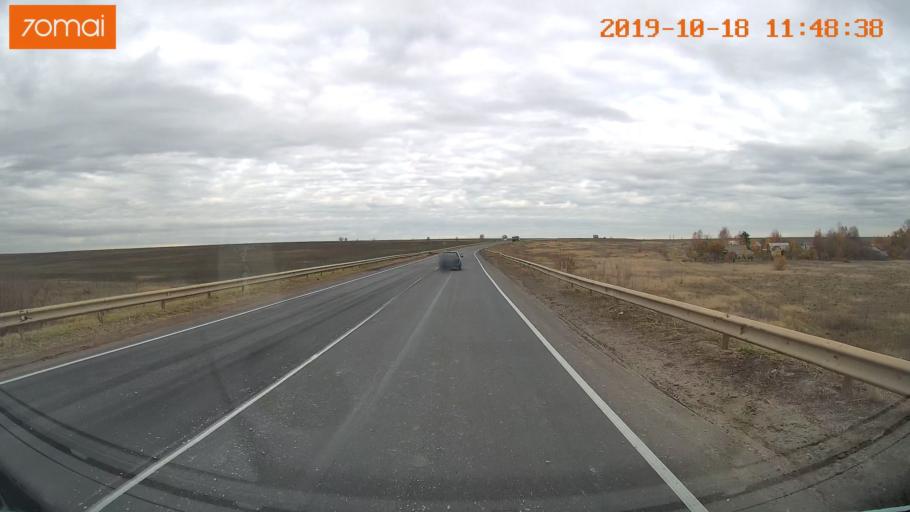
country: RU
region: Rjazan
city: Mikhaylov
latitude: 54.2408
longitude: 38.9842
